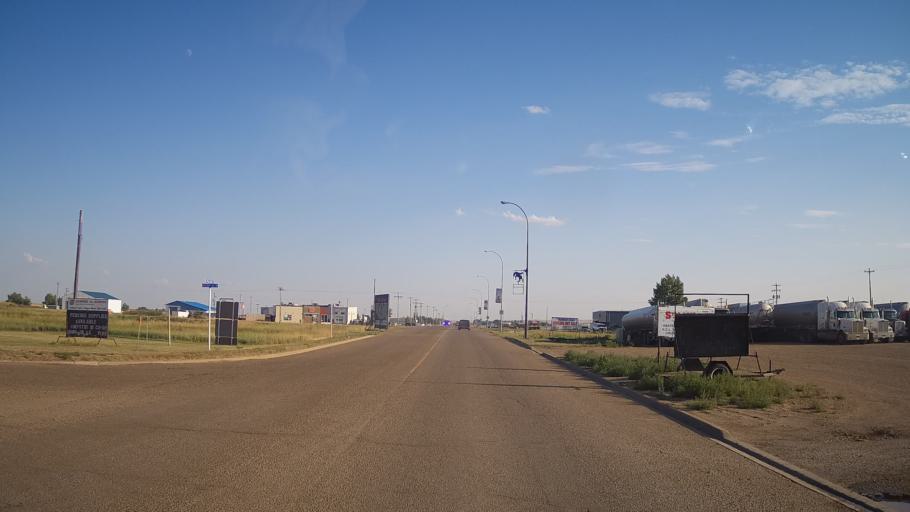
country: CA
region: Alberta
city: Hanna
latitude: 51.6386
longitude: -111.9422
